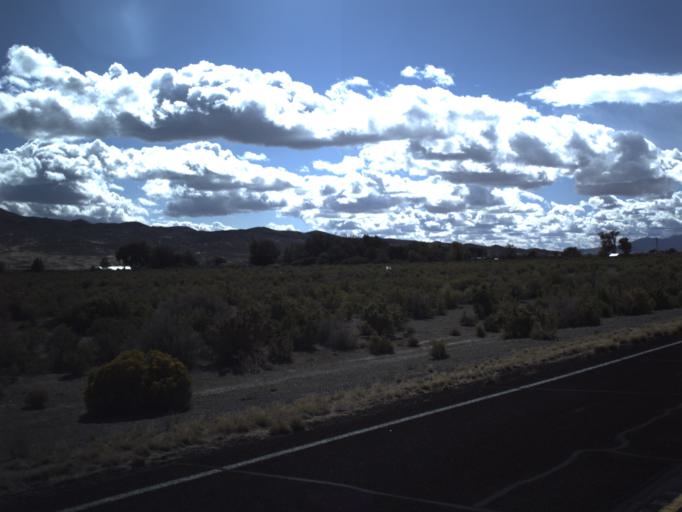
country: US
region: Nevada
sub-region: White Pine County
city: McGill
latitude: 38.9448
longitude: -114.0332
